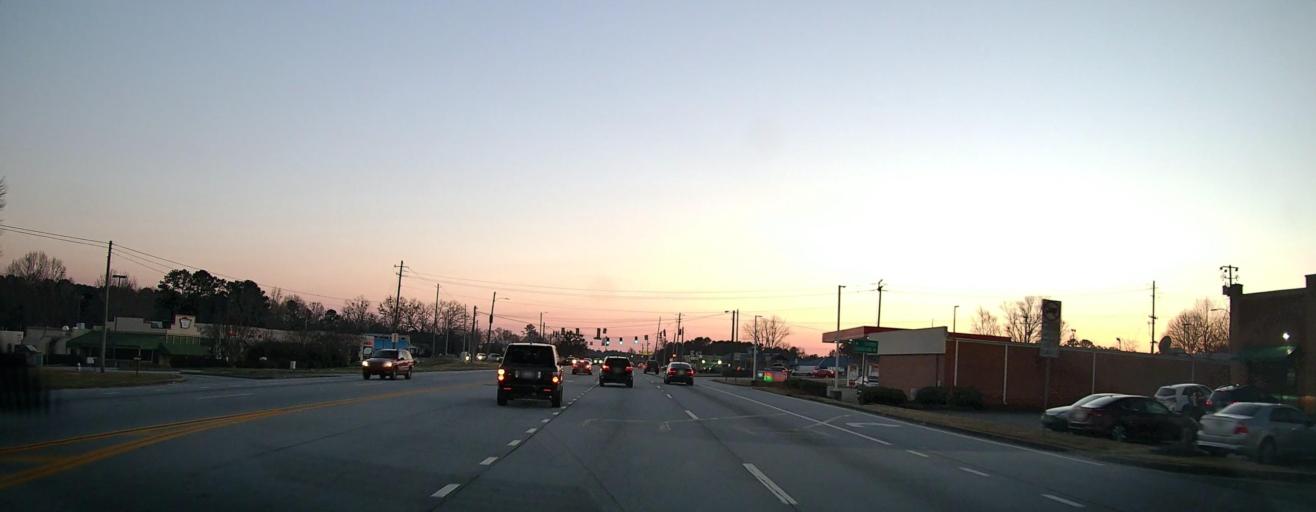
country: US
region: Georgia
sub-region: Fayette County
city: Fayetteville
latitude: 33.4651
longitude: -84.4490
